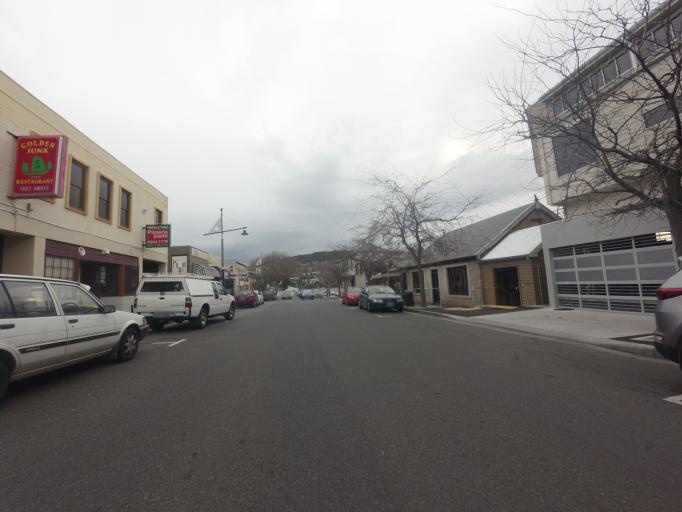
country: AU
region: Tasmania
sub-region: Clarence
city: Bellerive
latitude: -42.8747
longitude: 147.3662
